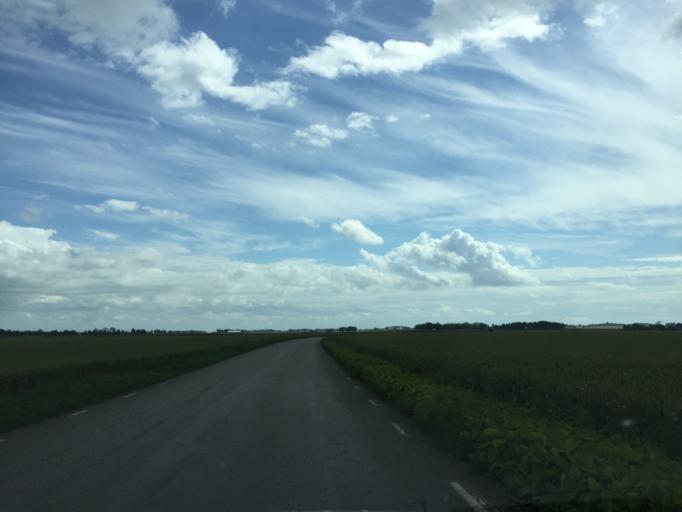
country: SE
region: OEstergoetland
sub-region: Vadstena Kommun
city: Vadstena
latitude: 58.4599
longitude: 14.8370
